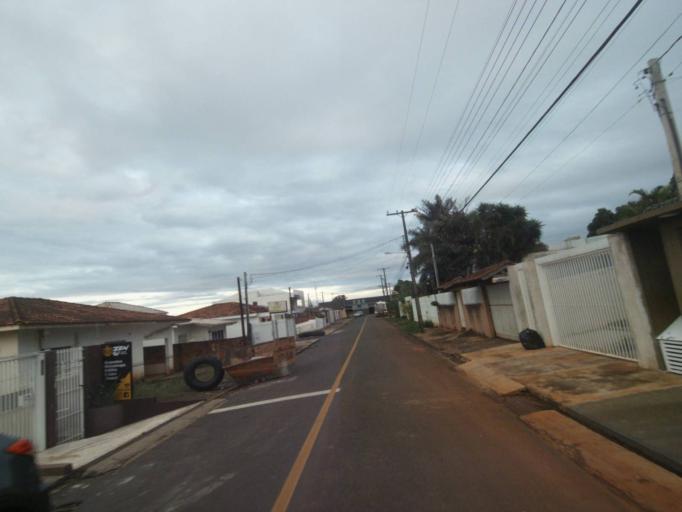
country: BR
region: Parana
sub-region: Telemaco Borba
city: Telemaco Borba
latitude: -24.3321
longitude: -50.6315
